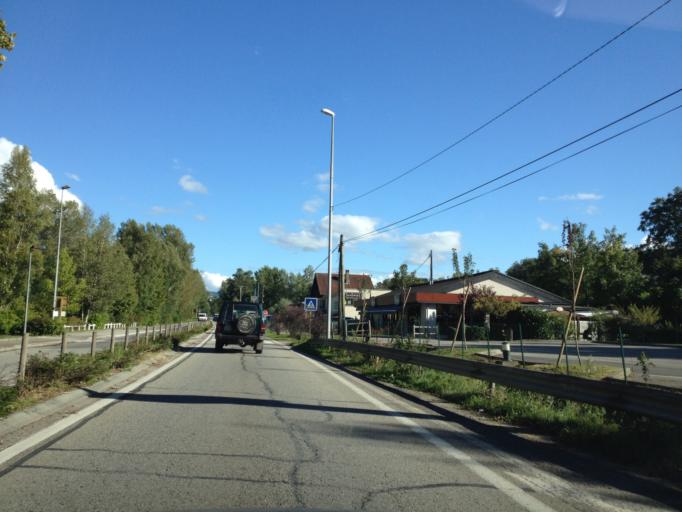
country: FR
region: Rhone-Alpes
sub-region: Departement de la Savoie
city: Le Bourget-du-Lac
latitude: 45.6419
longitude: 5.8646
